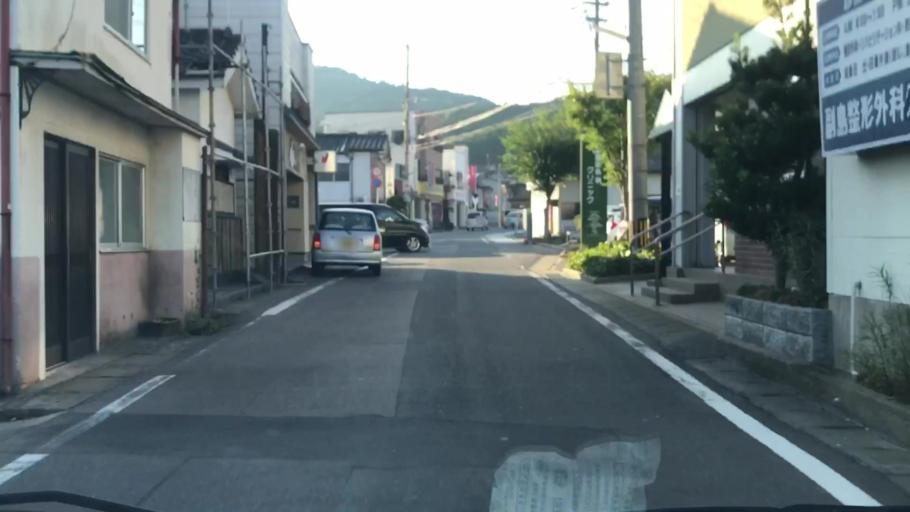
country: JP
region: Saga Prefecture
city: Takeocho-takeo
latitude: 33.1957
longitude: 130.0197
